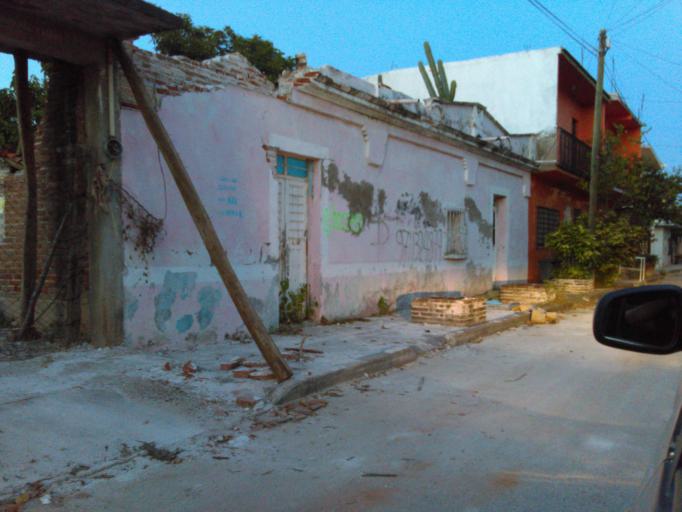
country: MX
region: Oaxaca
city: San Jeronimo Ixtepec
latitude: 16.5686
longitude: -95.0969
